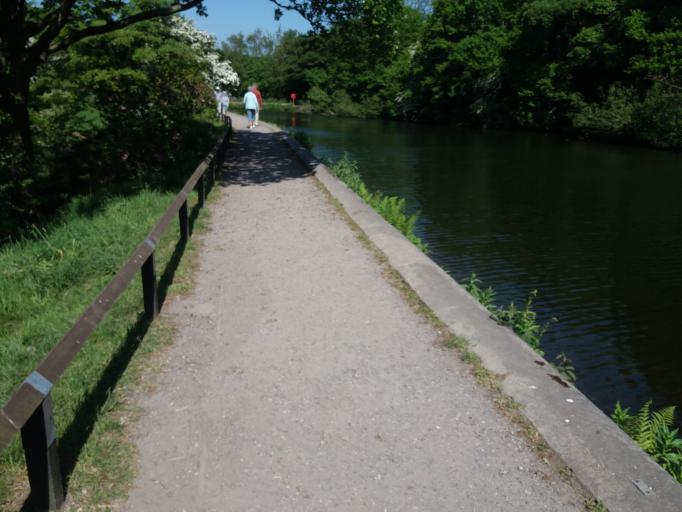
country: GB
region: England
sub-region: Lancashire
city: Coppull
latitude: 53.6308
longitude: -2.6494
